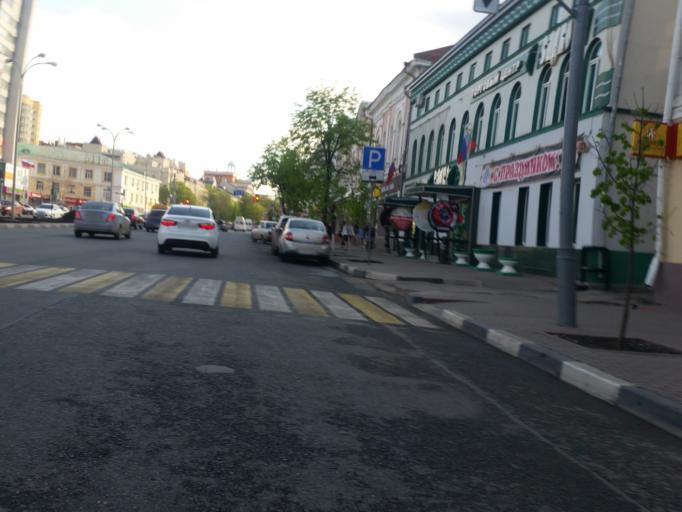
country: RU
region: Ulyanovsk
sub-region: Ulyanovskiy Rayon
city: Ulyanovsk
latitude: 54.3175
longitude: 48.3969
